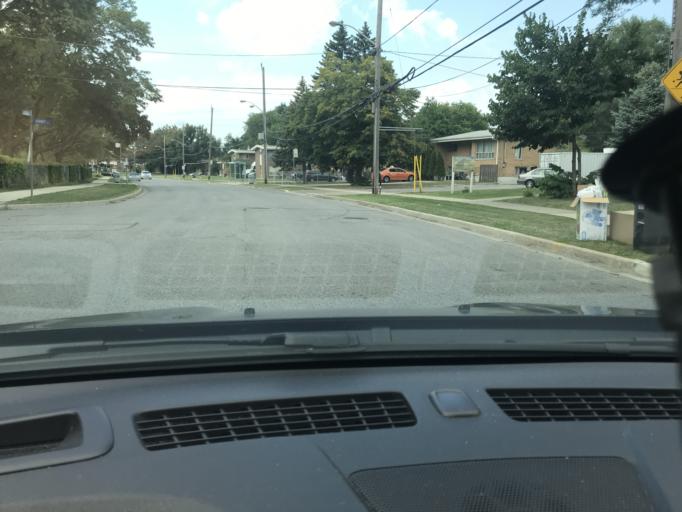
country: CA
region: Ontario
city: Toronto
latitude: 43.7207
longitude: -79.4409
